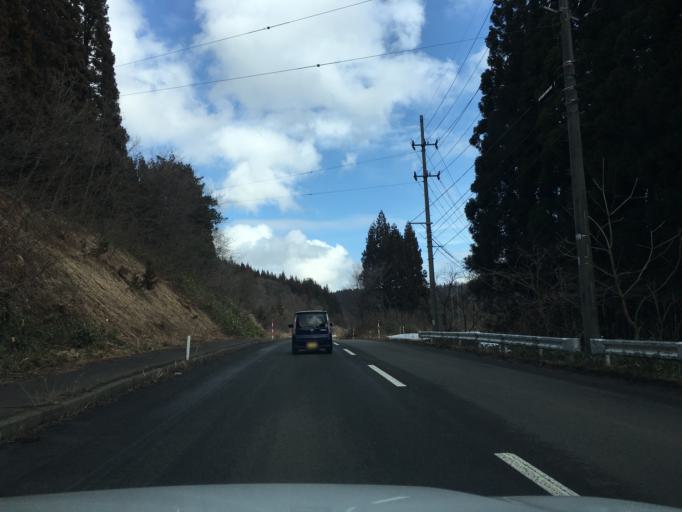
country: JP
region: Akita
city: Takanosu
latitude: 40.0879
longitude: 140.3312
